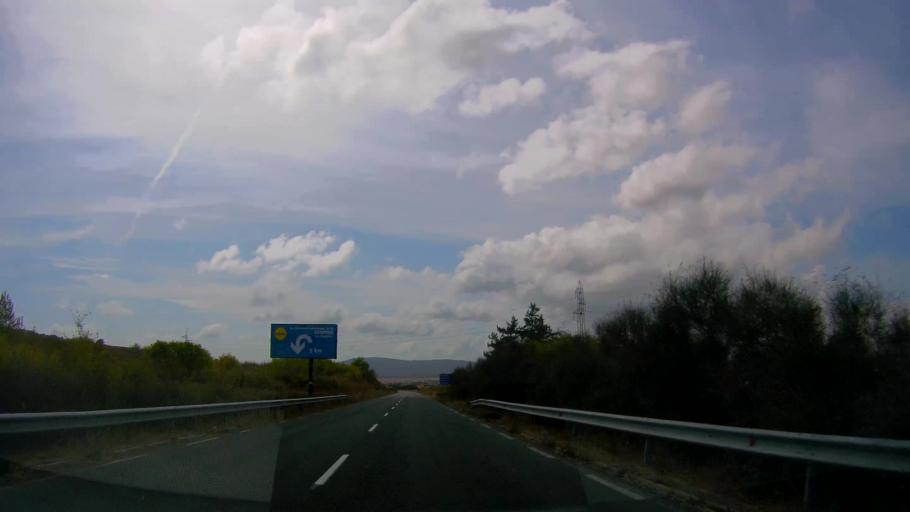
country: BG
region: Burgas
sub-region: Obshtina Sozopol
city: Sozopol
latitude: 42.3994
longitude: 27.6754
